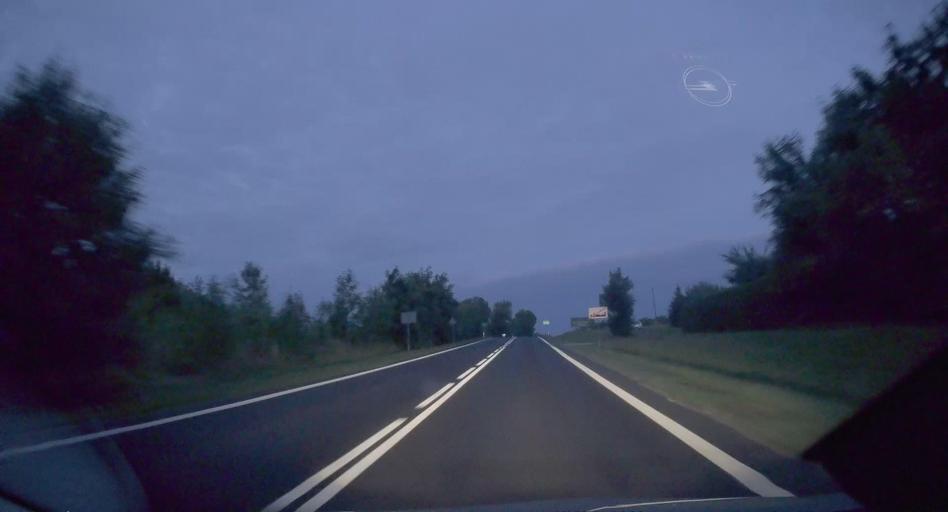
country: PL
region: Silesian Voivodeship
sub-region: Powiat klobucki
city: Kamyk
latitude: 50.8821
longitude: 18.9904
